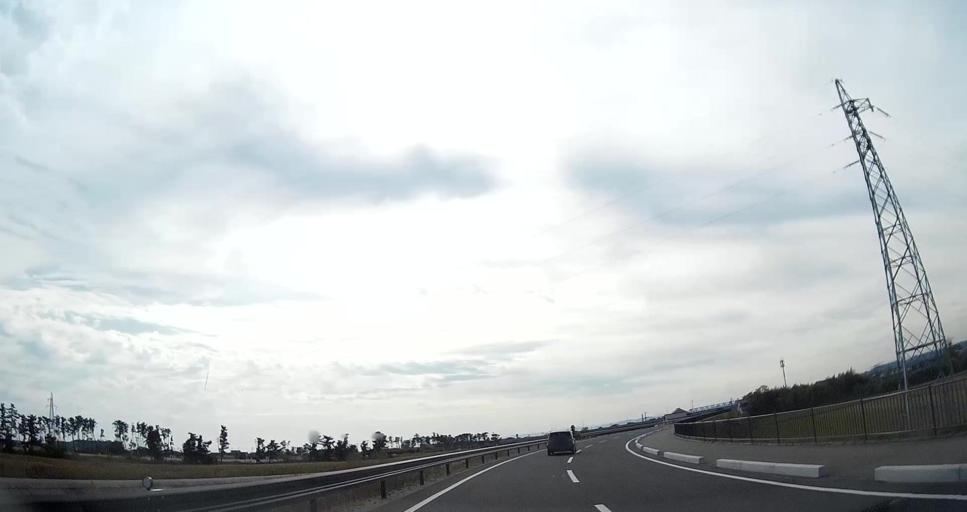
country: JP
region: Miyagi
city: Iwanuma
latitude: 38.1604
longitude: 140.9318
